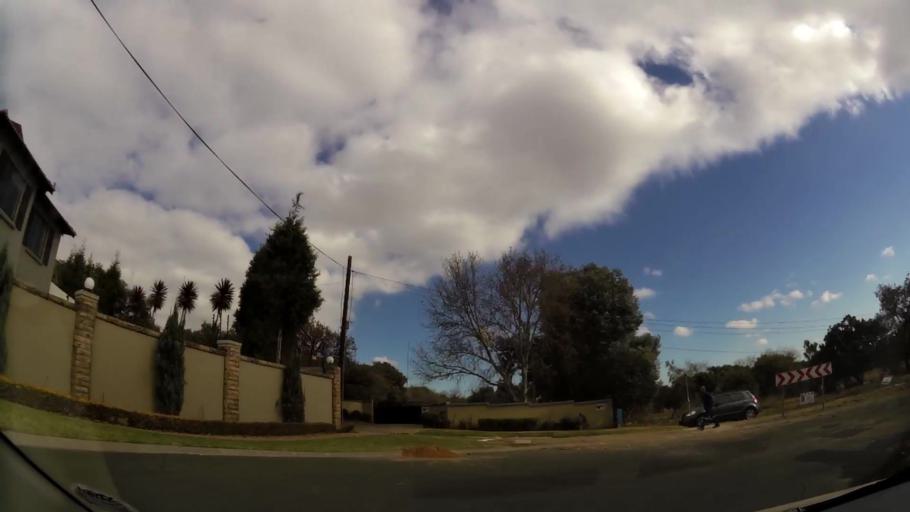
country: ZA
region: Gauteng
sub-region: City of Johannesburg Metropolitan Municipality
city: Roodepoort
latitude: -26.0969
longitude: 27.8667
